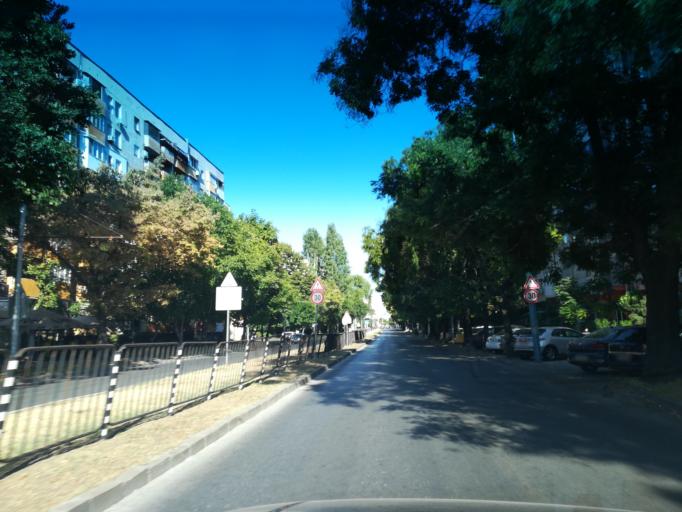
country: BG
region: Plovdiv
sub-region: Obshtina Plovdiv
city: Plovdiv
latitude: 42.1624
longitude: 24.7390
